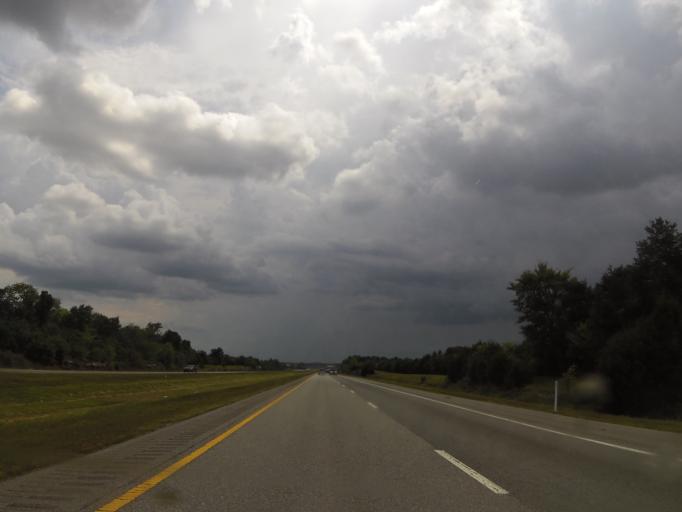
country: US
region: Tennessee
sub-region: Wilson County
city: Rural Hill
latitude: 36.0808
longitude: -86.4286
